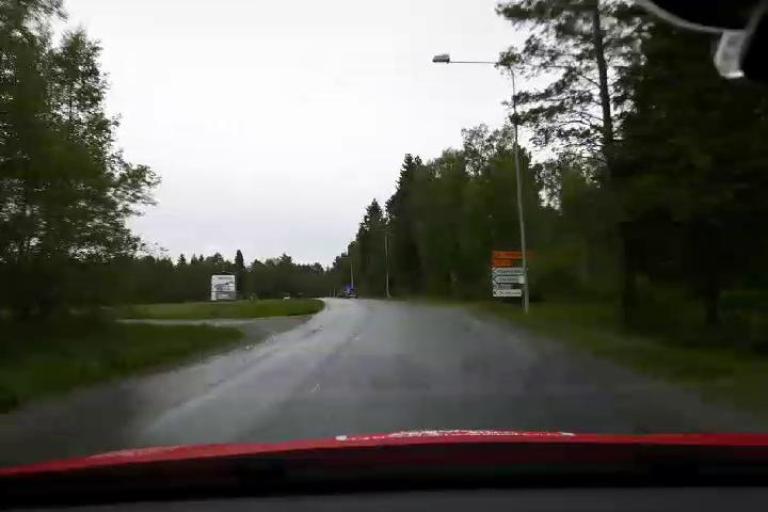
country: SE
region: Jaemtland
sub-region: Bergs Kommun
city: Hoverberg
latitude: 62.7732
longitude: 14.4301
